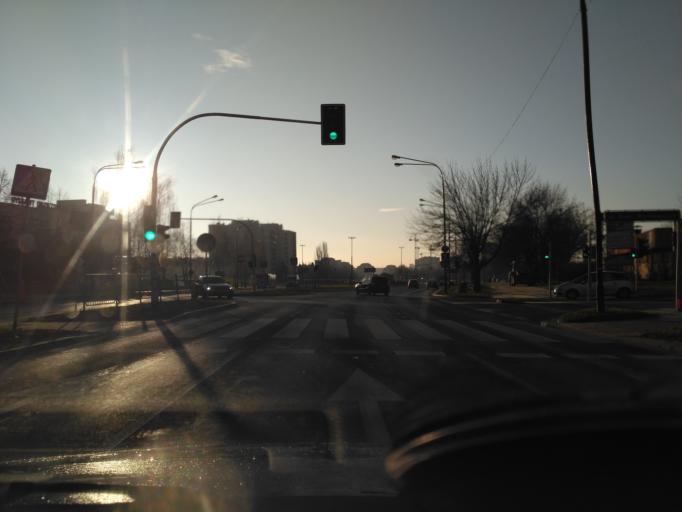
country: PL
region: Lublin Voivodeship
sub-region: Powiat lubelski
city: Lublin
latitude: 51.2646
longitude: 22.5510
